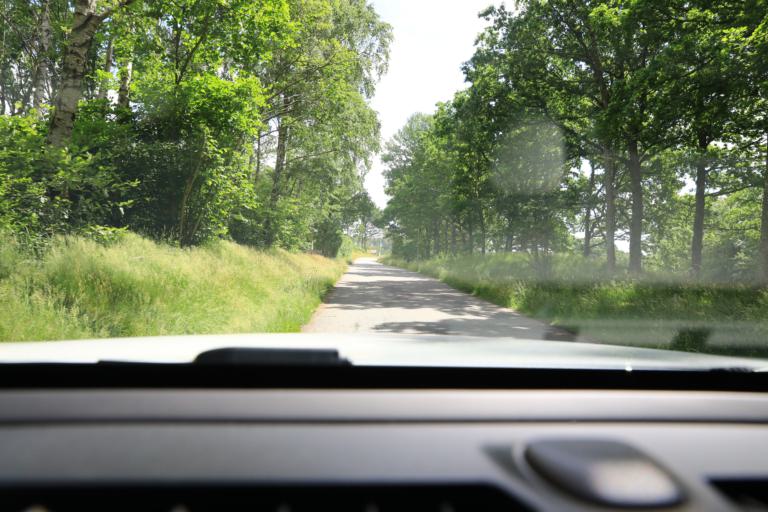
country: SE
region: Halland
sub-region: Varbergs Kommun
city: Tvaaker
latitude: 57.1060
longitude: 12.4501
